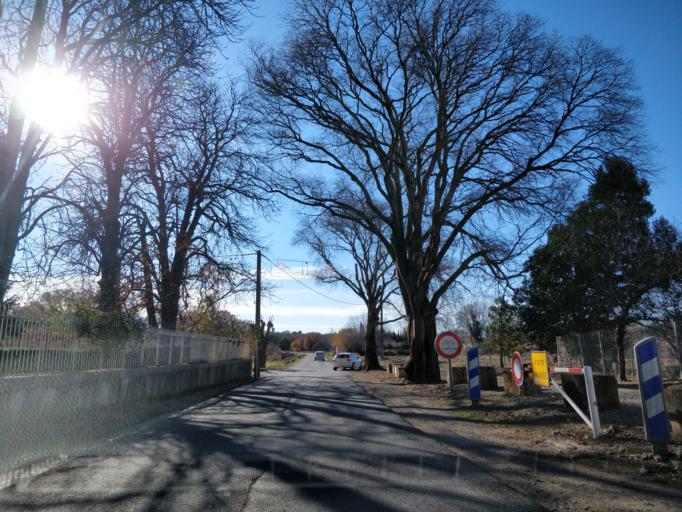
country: FR
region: Languedoc-Roussillon
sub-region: Departement de l'Herault
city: Beaulieu
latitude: 43.7677
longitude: 4.0198
